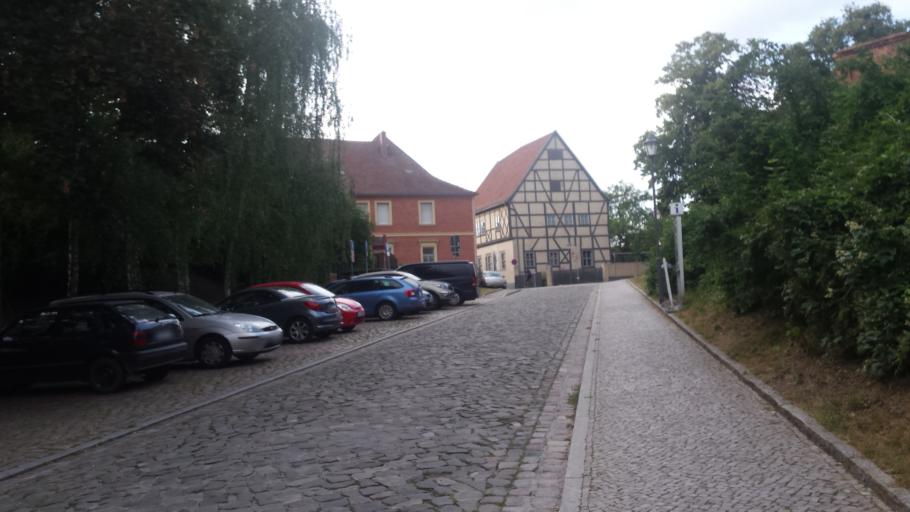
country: DE
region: Saxony-Anhalt
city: Tangermunde
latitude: 52.5429
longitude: 11.9770
